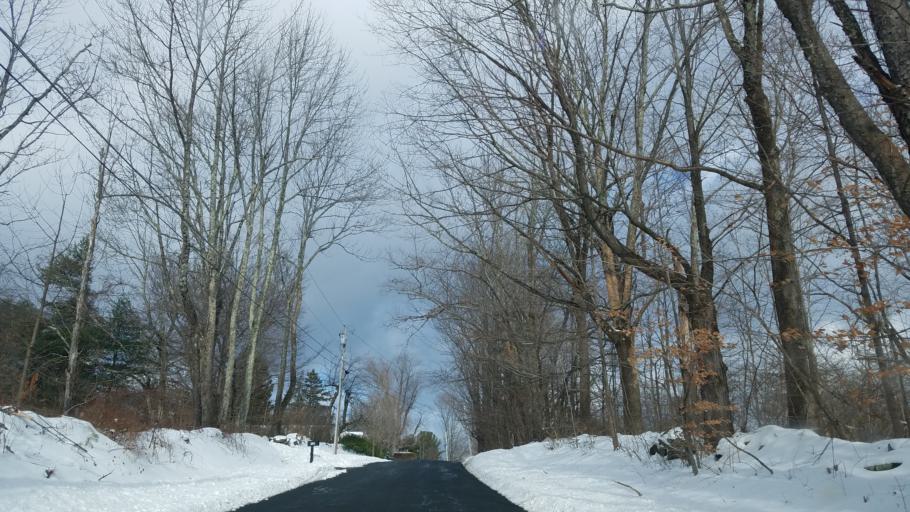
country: US
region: Connecticut
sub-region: Litchfield County
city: Winsted
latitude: 41.9689
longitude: -73.0756
